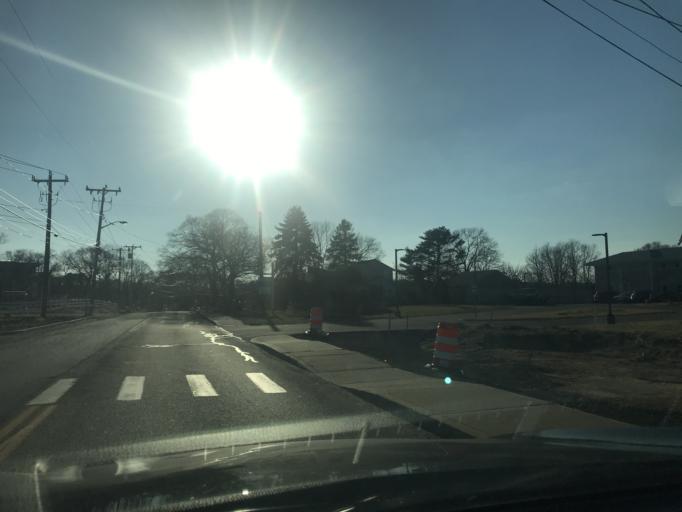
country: US
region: Massachusetts
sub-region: Plymouth County
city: Plymouth
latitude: 41.9399
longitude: -70.6528
